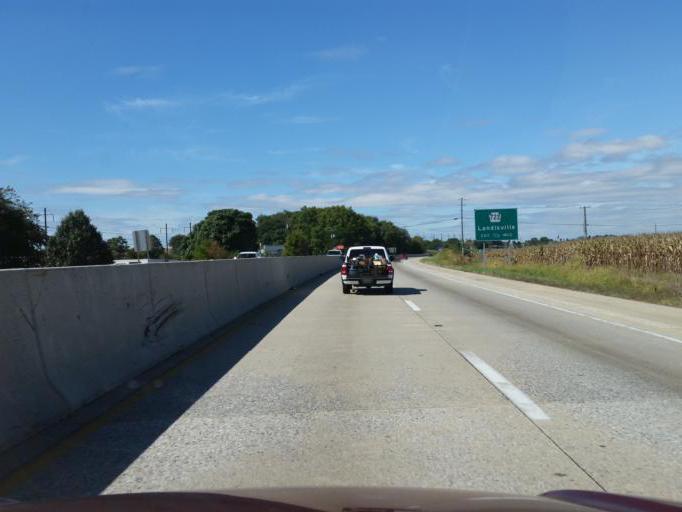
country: US
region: Pennsylvania
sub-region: Lancaster County
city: East Petersburg
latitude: 40.0840
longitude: -76.3690
